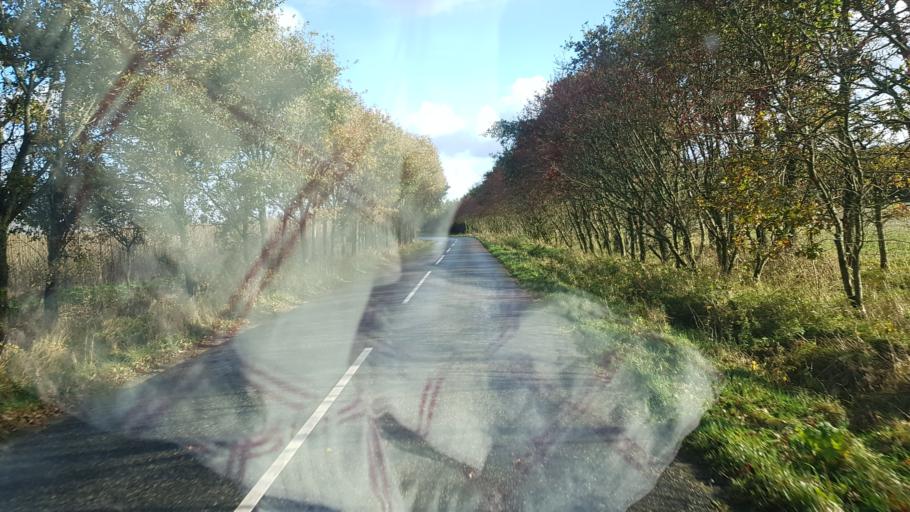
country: DK
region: South Denmark
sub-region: Varde Kommune
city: Olgod
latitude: 55.6976
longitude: 8.7244
